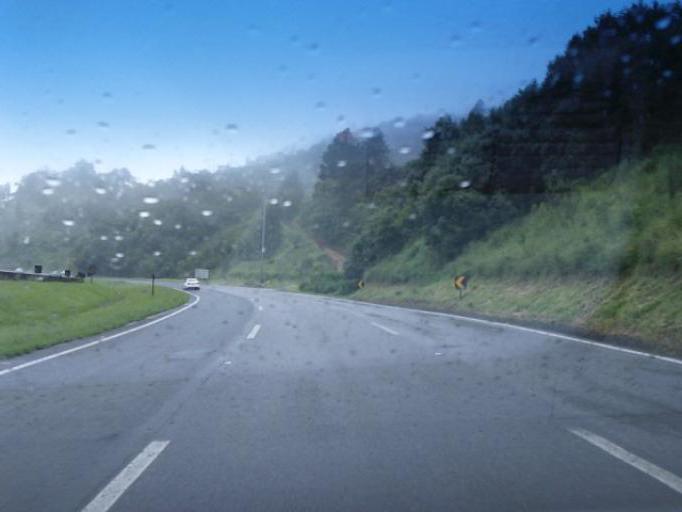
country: BR
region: Parana
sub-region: Campina Grande Do Sul
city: Campina Grande do Sul
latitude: -25.1641
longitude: -48.8619
